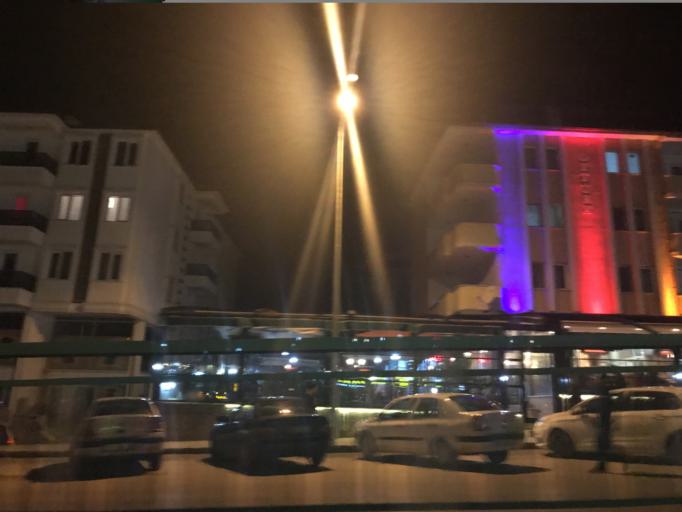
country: TR
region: Karabuk
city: Karabuk
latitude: 41.2192
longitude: 32.6603
